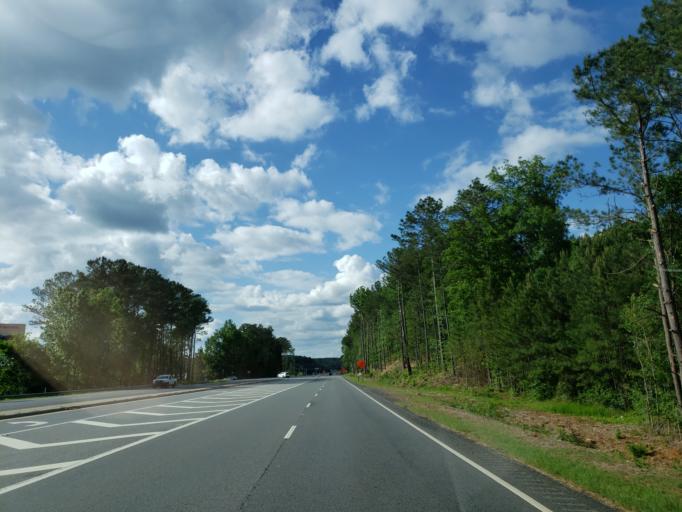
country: US
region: Georgia
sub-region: Bartow County
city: Cartersville
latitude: 34.2254
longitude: -84.8537
